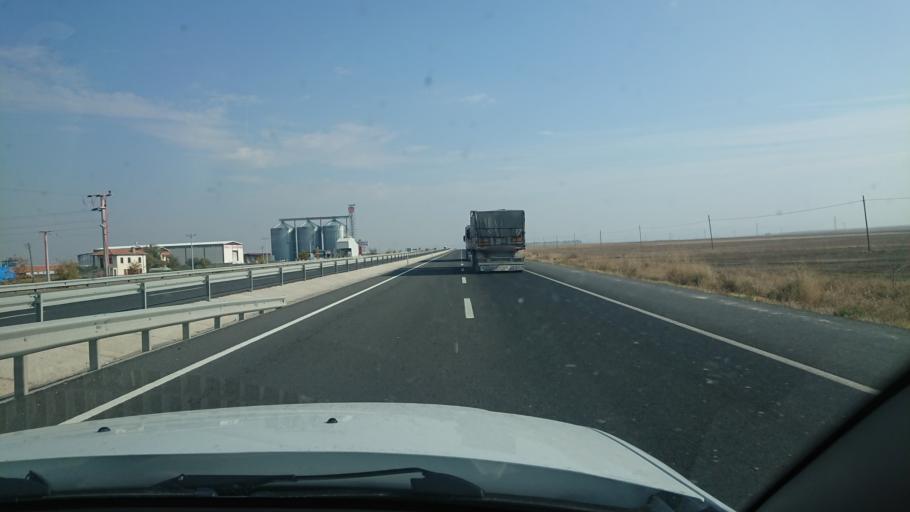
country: TR
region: Aksaray
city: Yesilova
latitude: 38.3270
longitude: 33.8911
